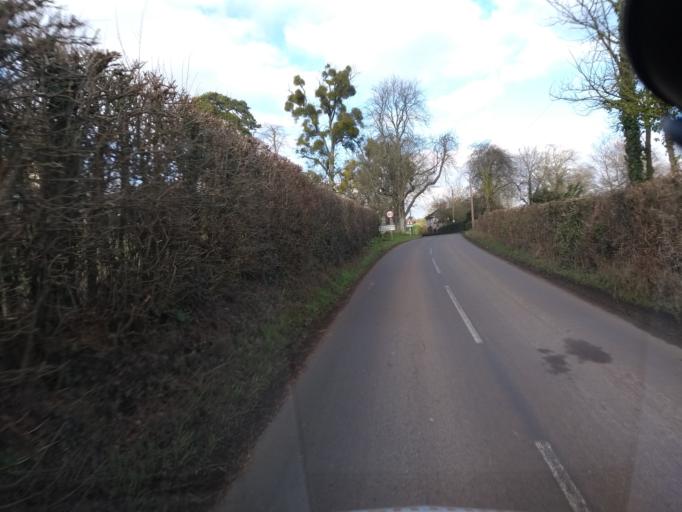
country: GB
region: England
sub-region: Somerset
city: Creech Saint Michael
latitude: 50.9580
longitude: -3.0482
